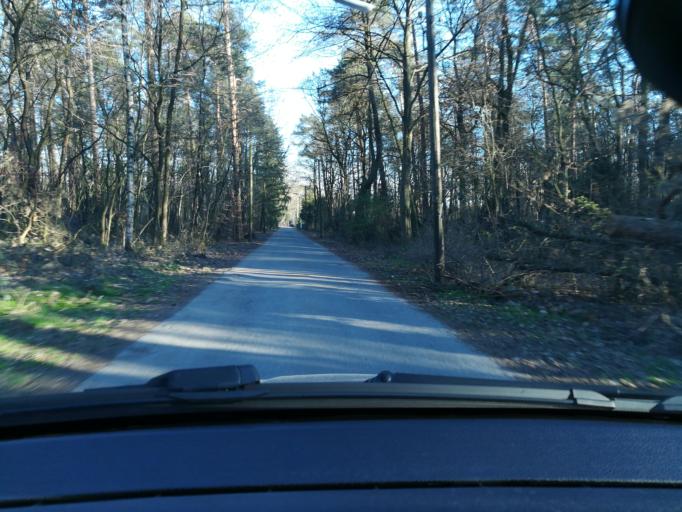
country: DE
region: North Rhine-Westphalia
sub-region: Regierungsbezirk Detmold
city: Oerlinghausen
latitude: 51.9500
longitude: 8.6005
